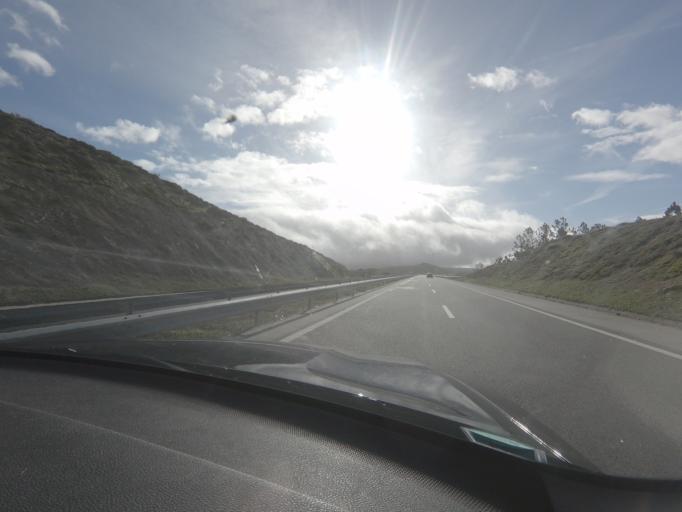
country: PT
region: Viseu
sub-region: Lamego
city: Lamego
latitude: 41.0396
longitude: -7.8598
